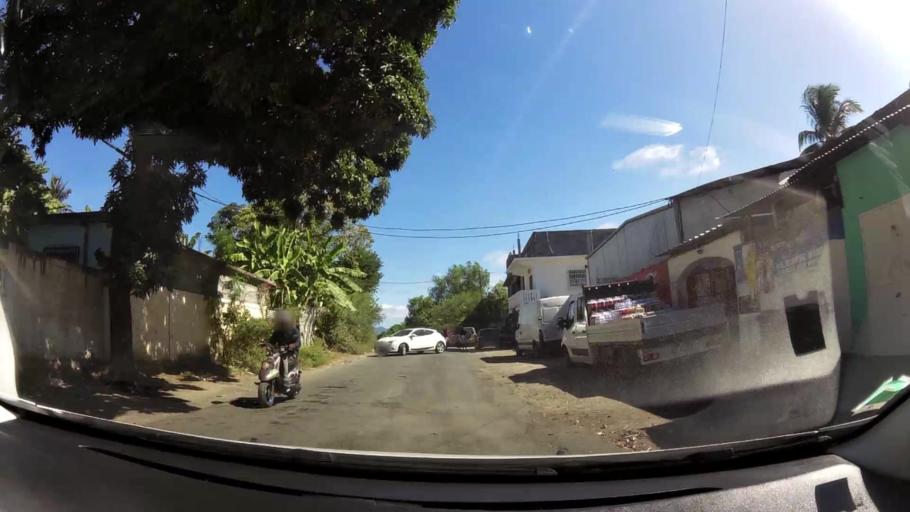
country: YT
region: Pamandzi
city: Pamandzi
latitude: -12.7824
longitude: 45.2769
